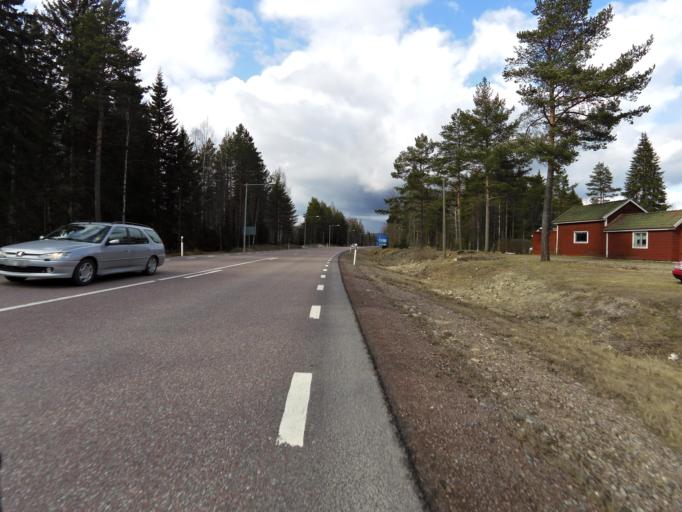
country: SE
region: Gaevleborg
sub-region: Hofors Kommun
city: Hofors
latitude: 60.4959
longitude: 16.4339
